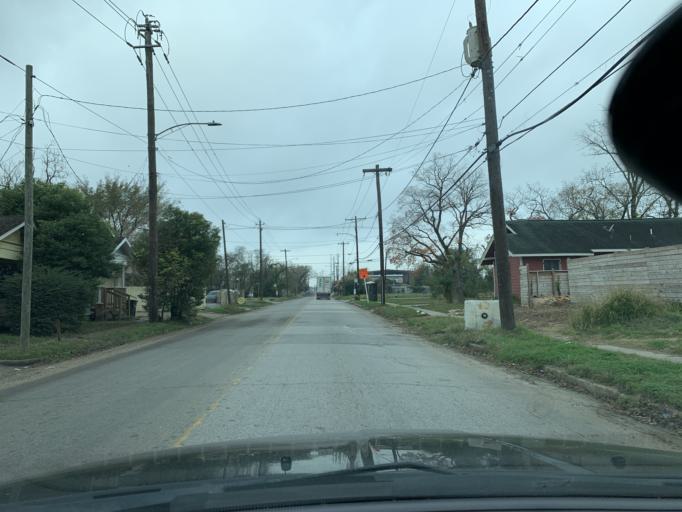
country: US
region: Texas
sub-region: Harris County
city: Houston
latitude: 29.7835
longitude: -95.3432
